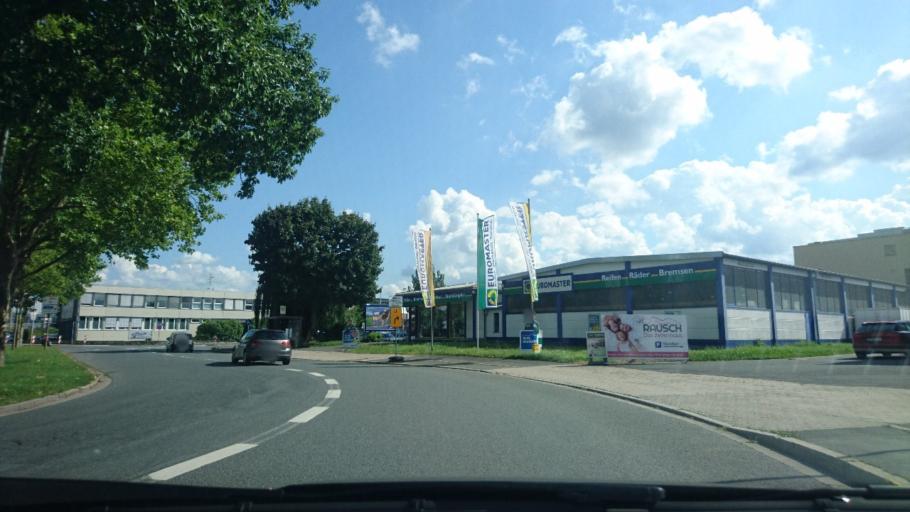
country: DE
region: Bavaria
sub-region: Upper Franconia
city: Bayreuth
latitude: 49.9602
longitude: 11.5985
